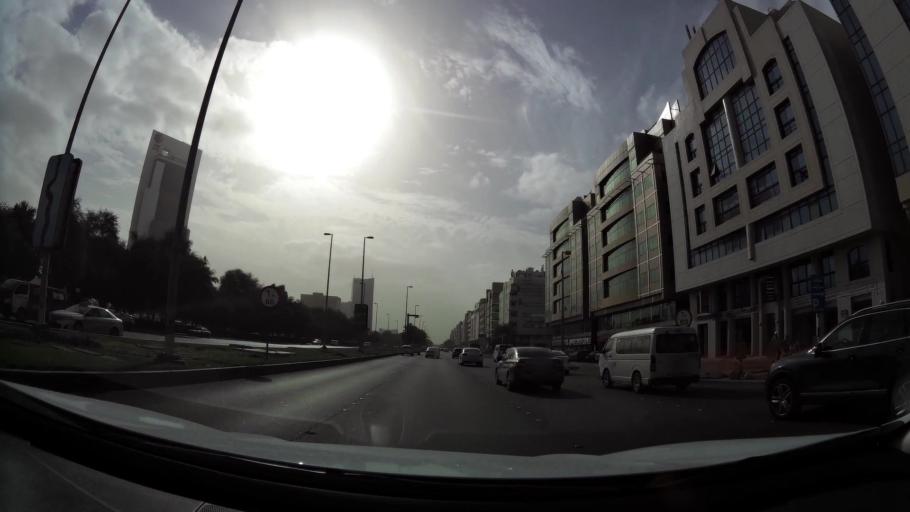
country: AE
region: Abu Dhabi
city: Abu Dhabi
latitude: 24.4609
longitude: 54.3873
